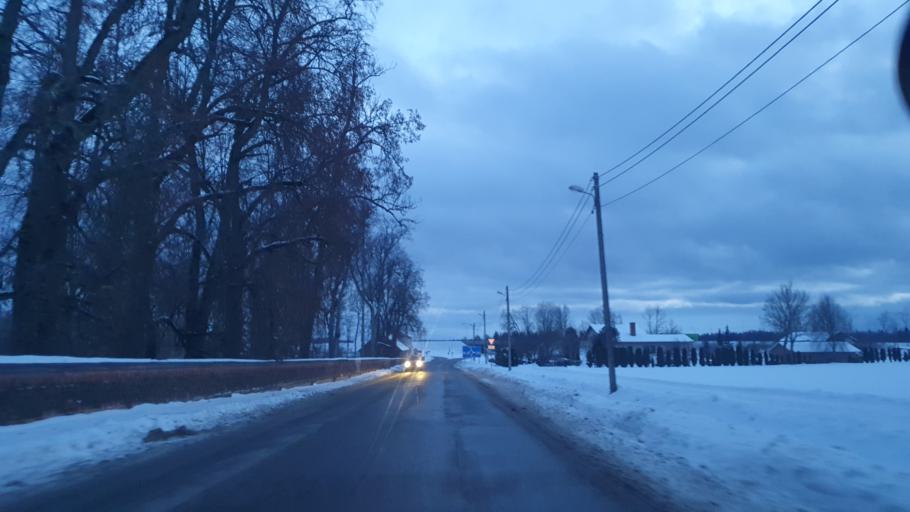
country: EE
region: Jogevamaa
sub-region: Jogeva linn
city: Jogeva
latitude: 58.5743
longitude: 26.2878
